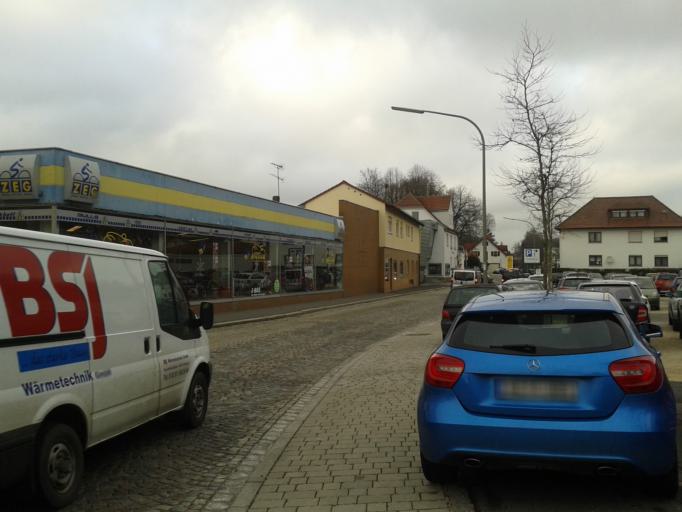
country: DE
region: Bavaria
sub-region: Upper Franconia
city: Kronach
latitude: 50.2430
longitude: 11.3236
